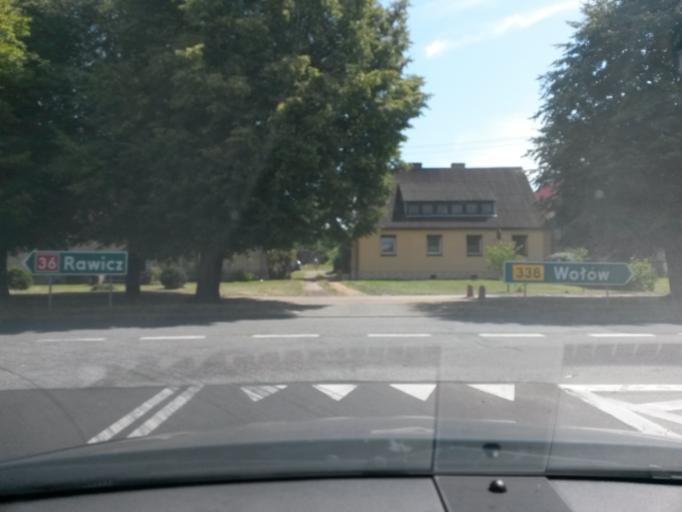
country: PL
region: Lower Silesian Voivodeship
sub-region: Powiat wolowski
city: Winsko
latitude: 51.4658
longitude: 16.6136
